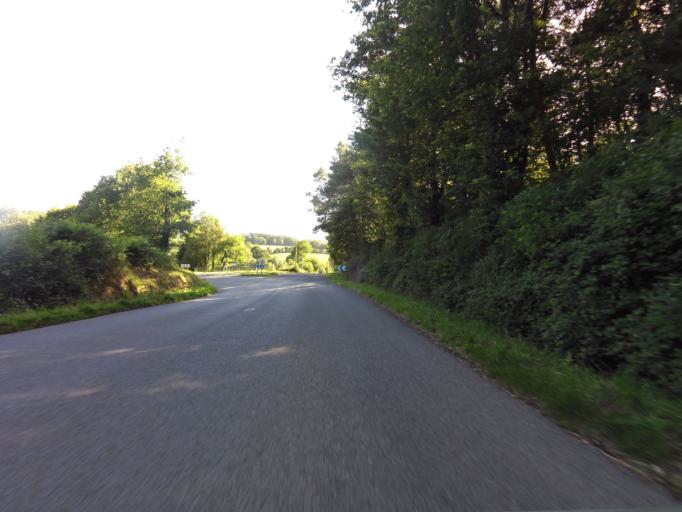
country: FR
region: Brittany
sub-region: Departement du Morbihan
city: Limerzel
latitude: 47.6300
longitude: -2.3542
